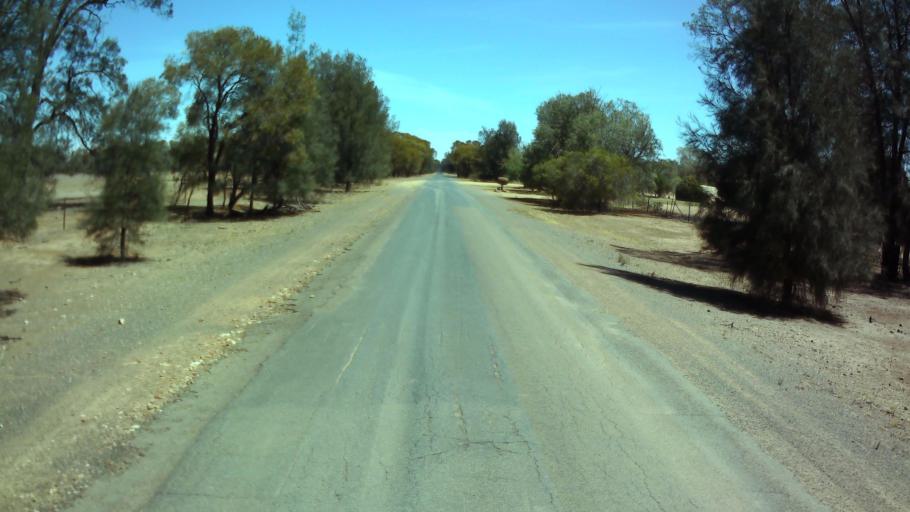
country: AU
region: New South Wales
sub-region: Weddin
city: Grenfell
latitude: -33.8698
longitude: 147.6921
